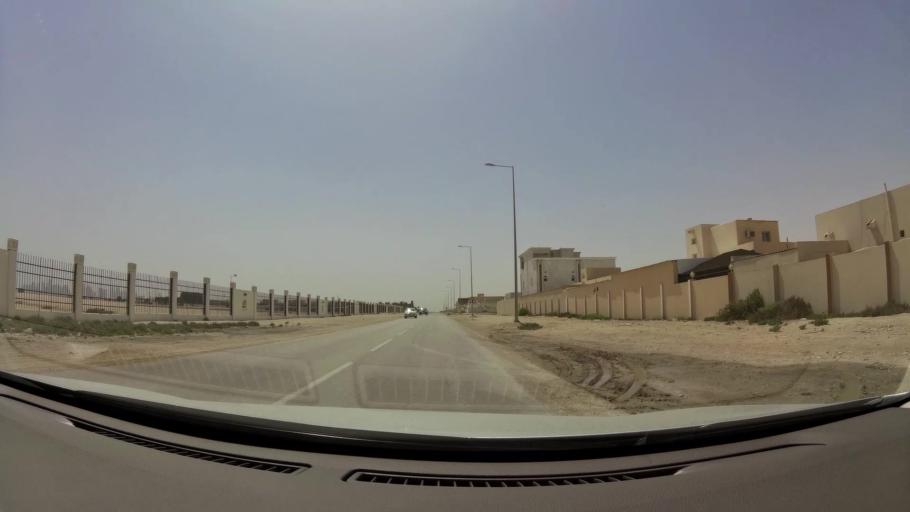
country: QA
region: Baladiyat Umm Salal
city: Umm Salal Muhammad
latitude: 25.3665
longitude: 51.4790
